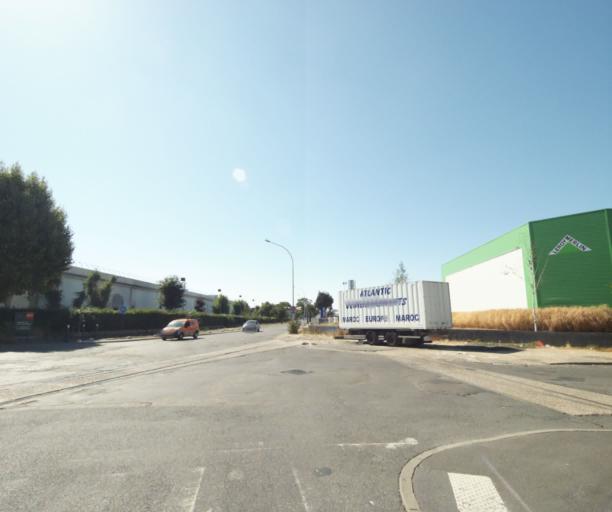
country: FR
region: Ile-de-France
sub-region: Departement des Hauts-de-Seine
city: Villeneuve-la-Garenne
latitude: 48.9275
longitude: 2.3190
